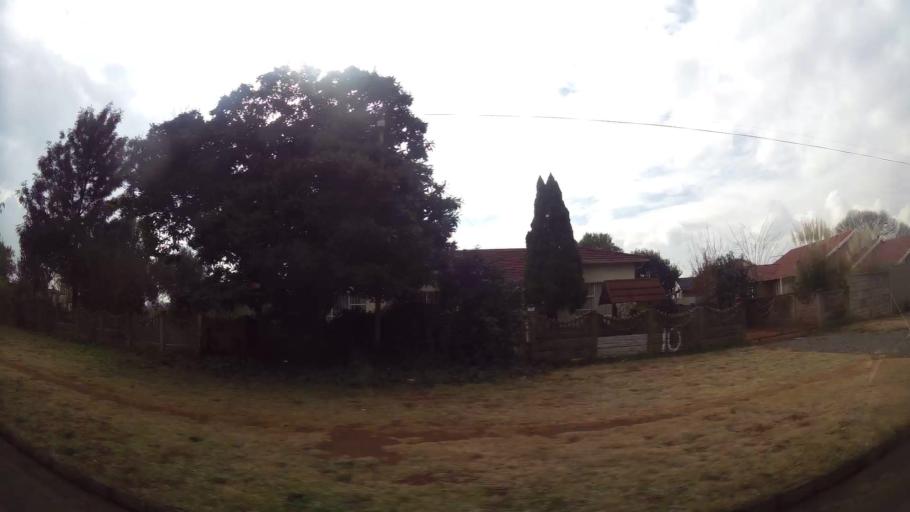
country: ZA
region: Gauteng
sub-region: Sedibeng District Municipality
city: Meyerton
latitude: -26.6002
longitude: 27.9950
